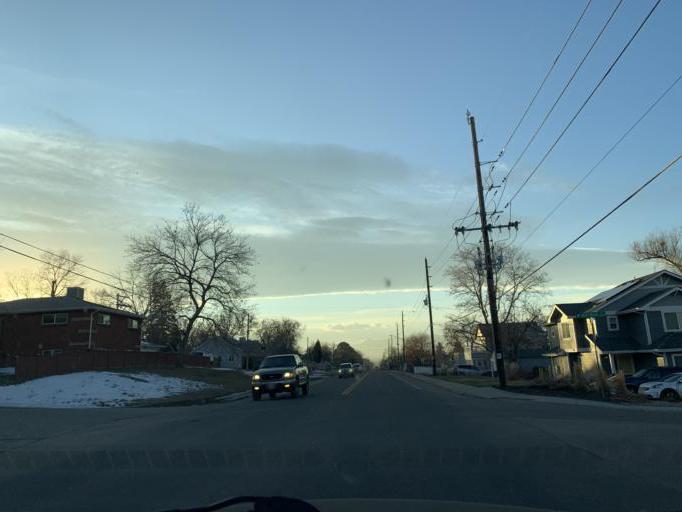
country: US
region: Colorado
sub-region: Adams County
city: Berkley
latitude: 39.7911
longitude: -105.0402
